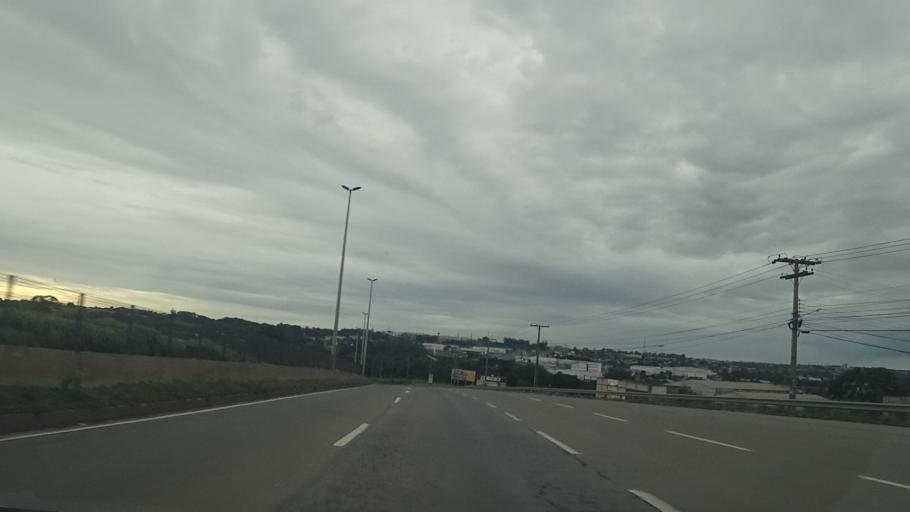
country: BR
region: Goias
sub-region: Aparecida De Goiania
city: Aparecida de Goiania
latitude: -16.7695
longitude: -49.2393
